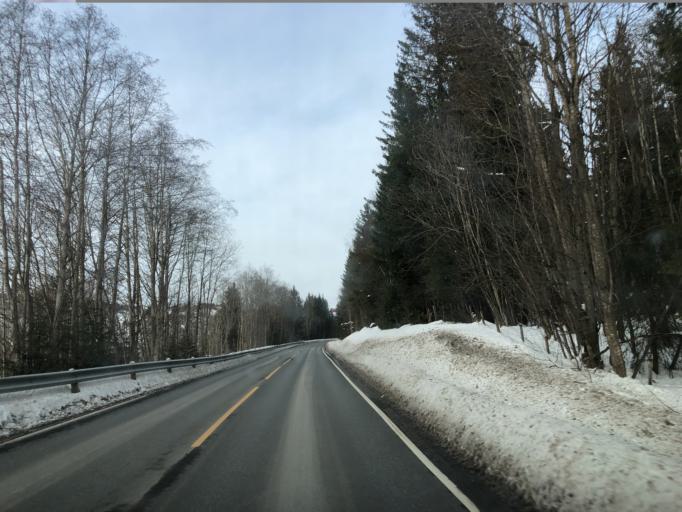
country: NO
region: Oppland
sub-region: Gausdal
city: Segalstad bru
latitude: 61.2755
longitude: 10.1465
